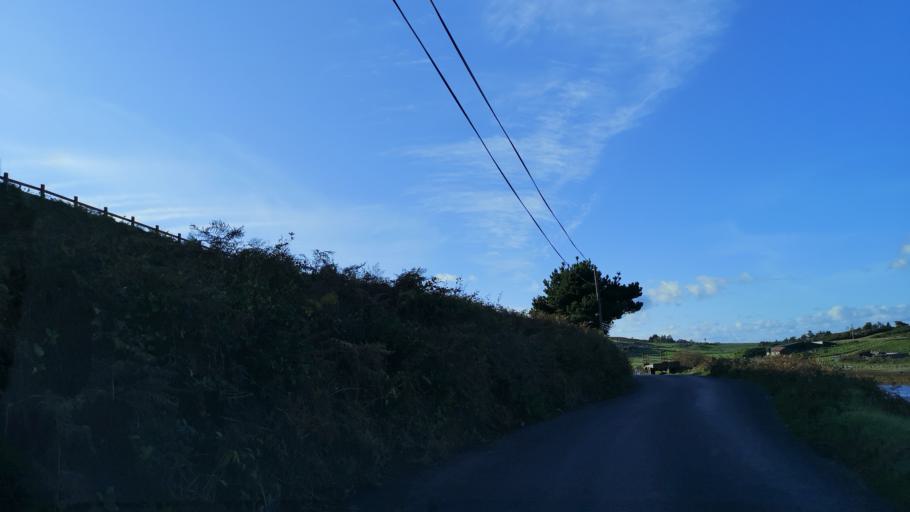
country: IE
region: Connaught
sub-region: County Galway
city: Clifden
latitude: 53.5060
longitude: -10.0788
